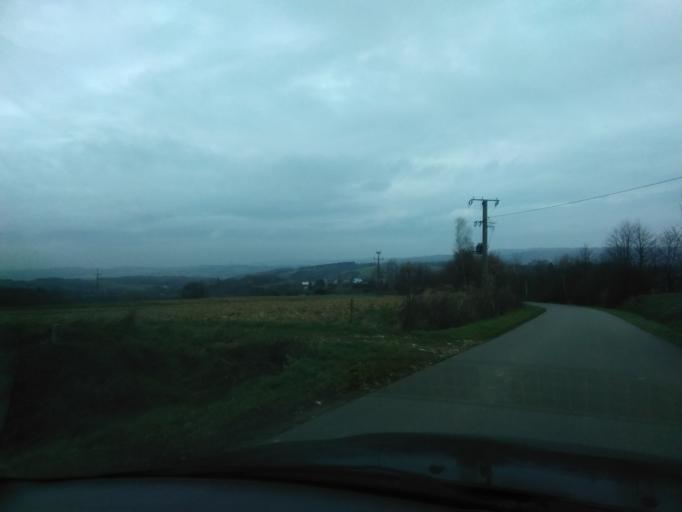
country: PL
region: Subcarpathian Voivodeship
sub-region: Powiat strzyzowski
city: Wysoka Strzyzowska
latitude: 49.8370
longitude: 21.7755
